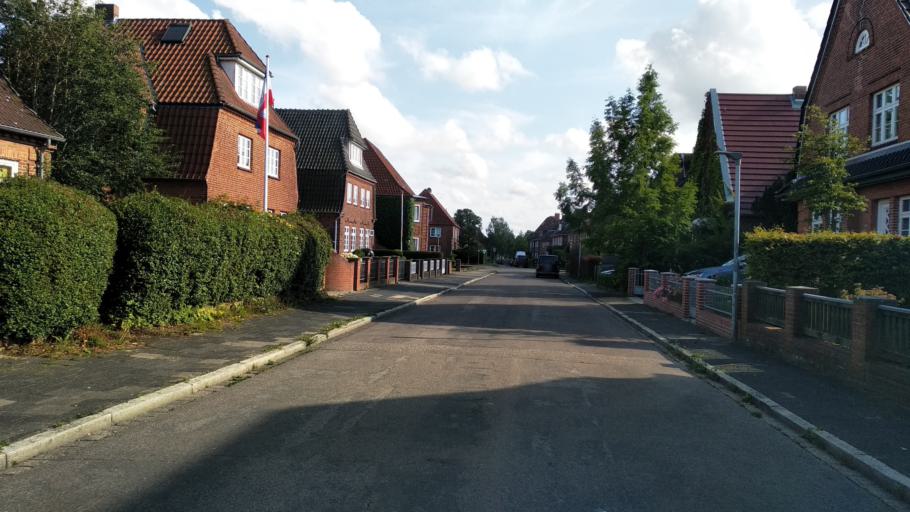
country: DE
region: Schleswig-Holstein
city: Schleswig
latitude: 54.5188
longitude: 9.5533
